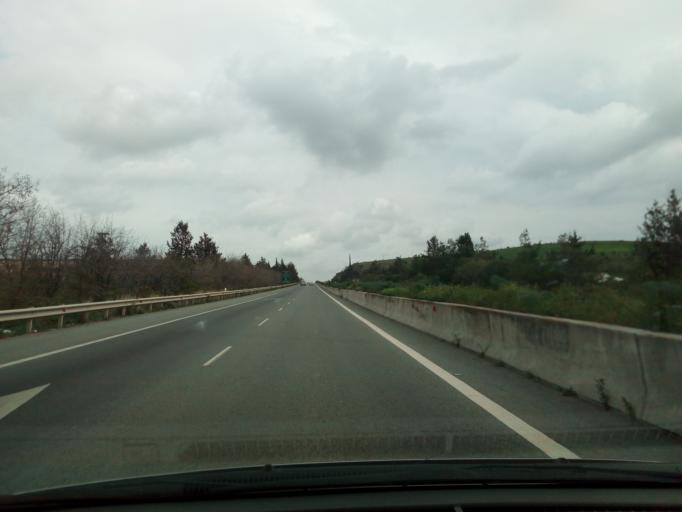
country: CY
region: Lefkosia
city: Alampra
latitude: 34.9990
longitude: 33.4174
